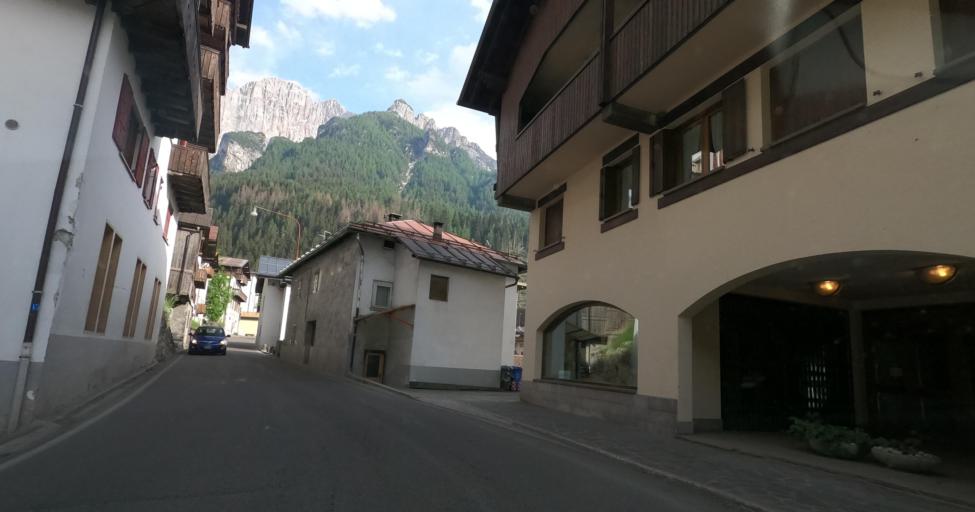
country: IT
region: Veneto
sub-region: Provincia di Belluno
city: Alleghe
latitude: 46.4077
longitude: 12.0196
